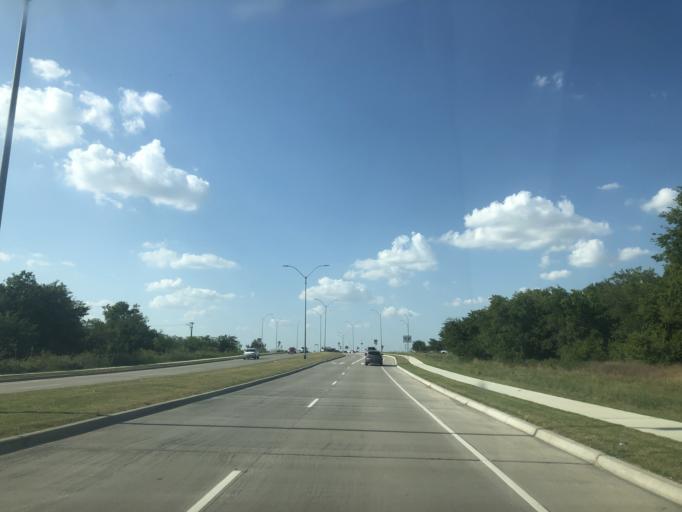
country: US
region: Texas
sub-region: Tarrant County
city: Saginaw
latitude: 32.8497
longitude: -97.3906
